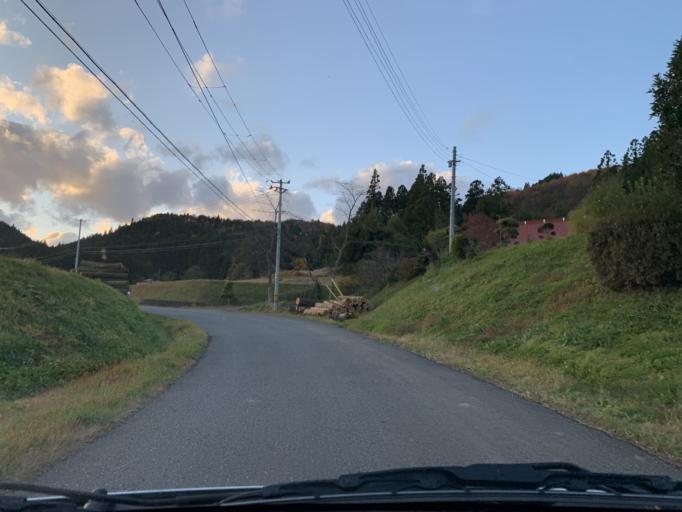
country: JP
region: Iwate
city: Mizusawa
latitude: 39.0323
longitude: 141.0439
